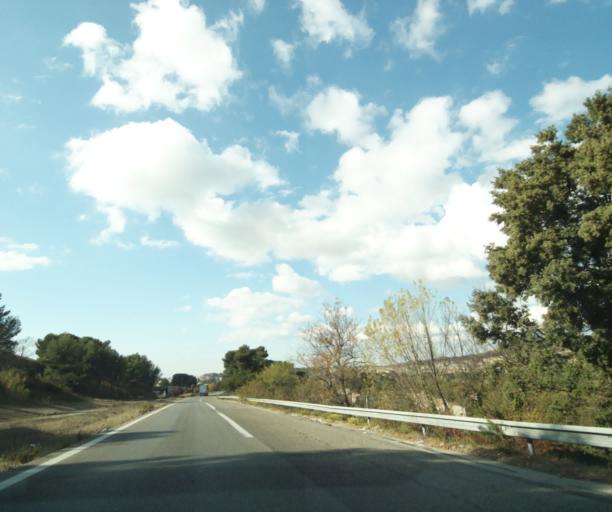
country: FR
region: Provence-Alpes-Cote d'Azur
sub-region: Departement des Bouches-du-Rhone
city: Les Pennes-Mirabeau
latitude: 43.4071
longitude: 5.3336
